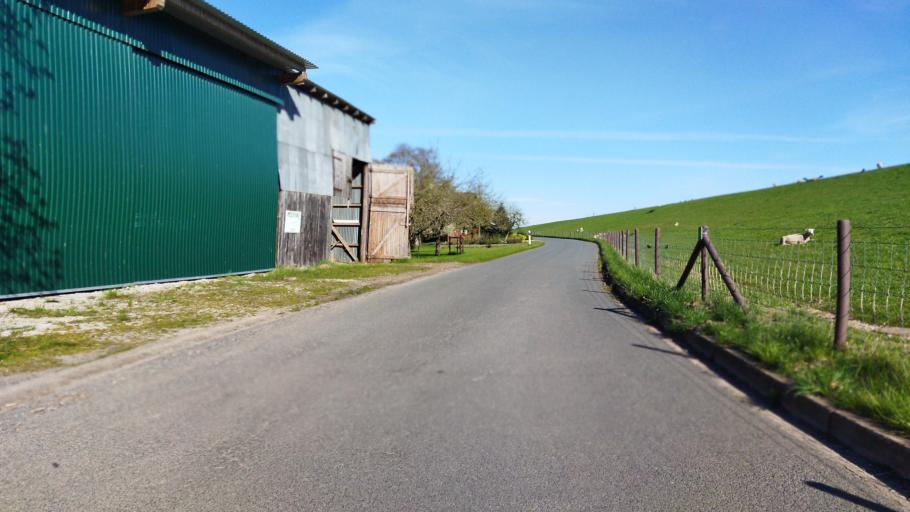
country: DE
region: Lower Saxony
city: Elsfleth
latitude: 53.2168
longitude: 8.4765
